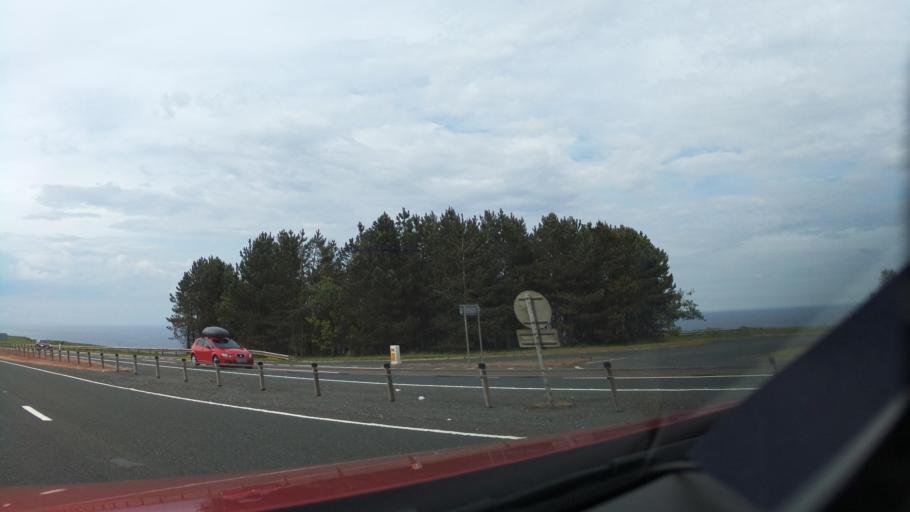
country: GB
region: England
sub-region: Northumberland
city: Berwick-Upon-Tweed
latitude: 55.8120
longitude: -2.0463
